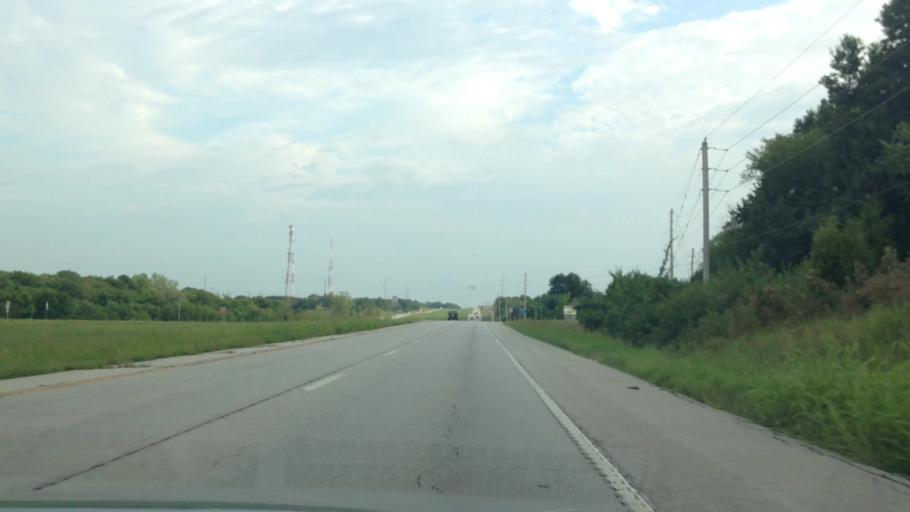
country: US
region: Missouri
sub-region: Clay County
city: Smithville
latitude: 39.3415
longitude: -94.5843
